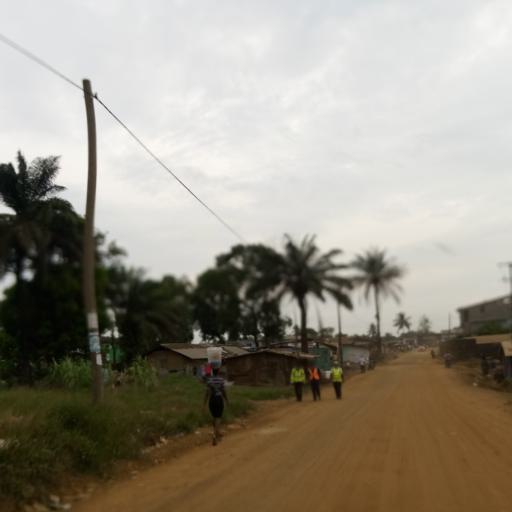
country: LR
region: Montserrado
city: Monrovia
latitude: 6.2965
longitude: -10.6807
